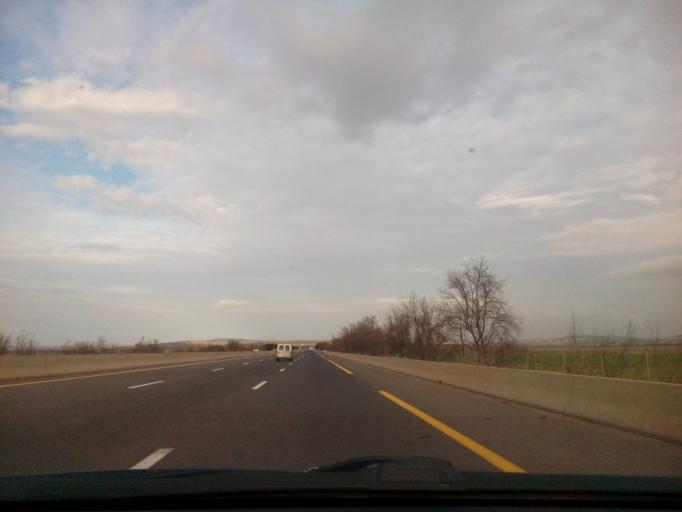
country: DZ
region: Mostaganem
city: Mostaganem
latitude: 35.6771
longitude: 0.1508
